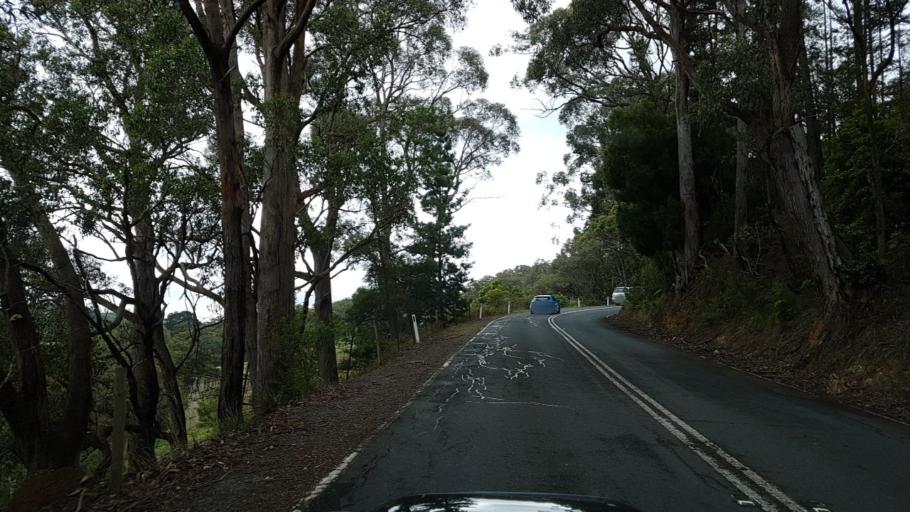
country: AU
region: South Australia
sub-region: Adelaide Hills
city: Bridgewater
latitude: -34.9418
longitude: 138.7764
